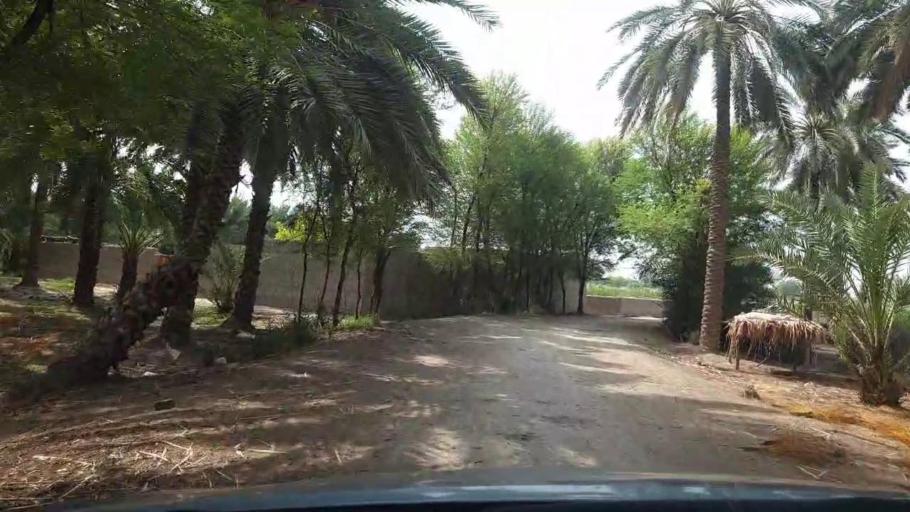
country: PK
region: Sindh
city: Rohri
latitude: 27.6530
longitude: 69.0105
